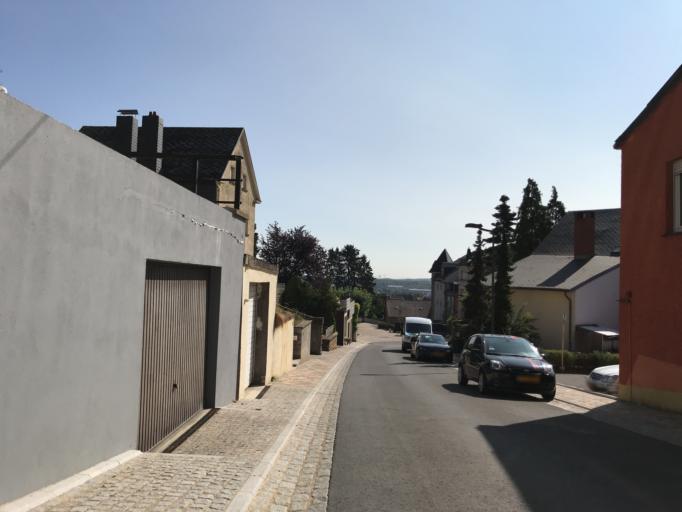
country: LU
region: Luxembourg
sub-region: Canton d'Esch-sur-Alzette
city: Niedercorn
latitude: 49.5382
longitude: 5.8894
